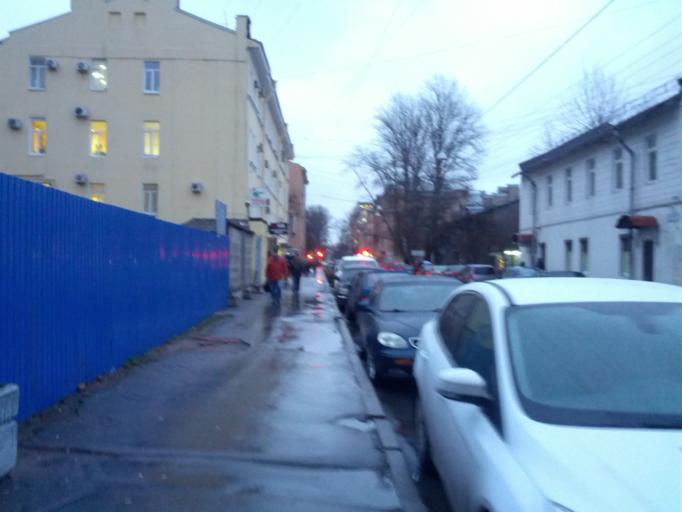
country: RU
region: St.-Petersburg
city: Admiralteisky
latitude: 59.8888
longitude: 30.3216
